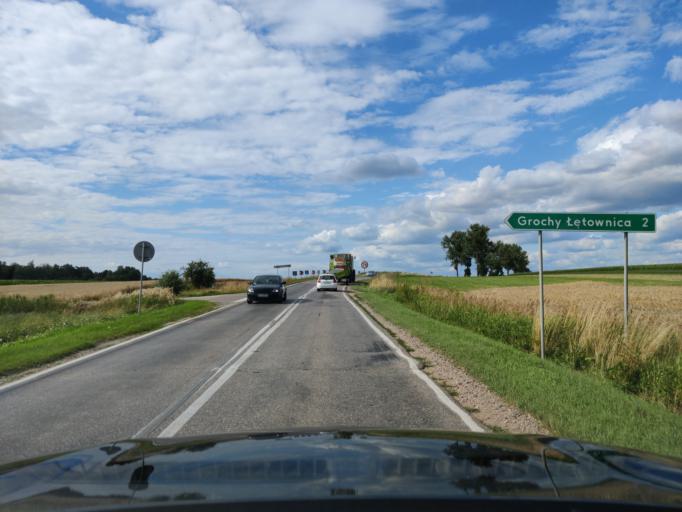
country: PL
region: Podlasie
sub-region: Powiat zambrowski
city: Zambrow
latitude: 52.8893
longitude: 22.2510
